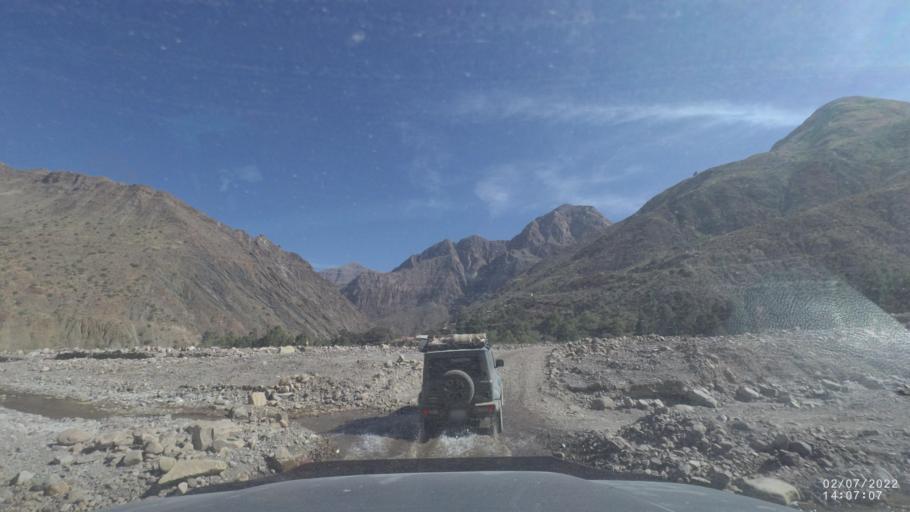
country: BO
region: Cochabamba
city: Irpa Irpa
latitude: -17.8188
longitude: -66.4001
